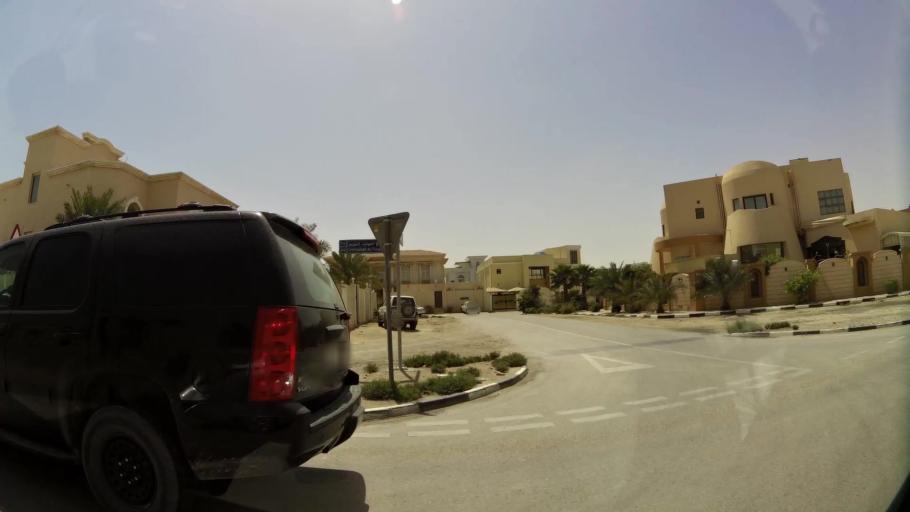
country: QA
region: Baladiyat Umm Salal
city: Umm Salal Muhammad
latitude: 25.3745
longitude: 51.4728
